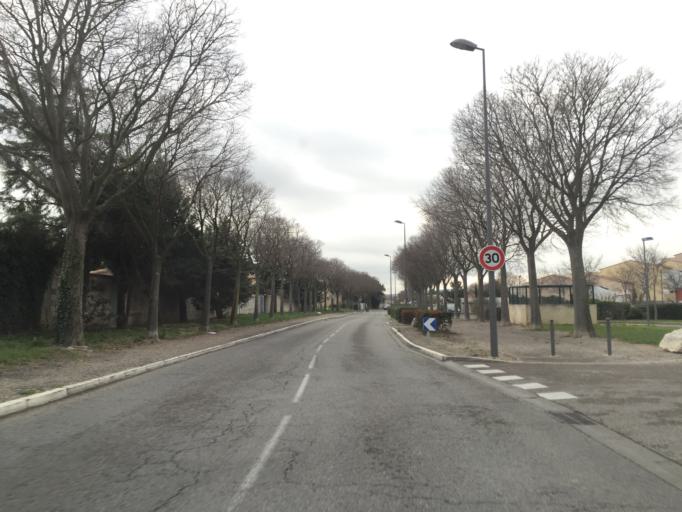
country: FR
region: Provence-Alpes-Cote d'Azur
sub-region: Departement du Vaucluse
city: Sorgues
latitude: 44.0171
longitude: 4.8627
